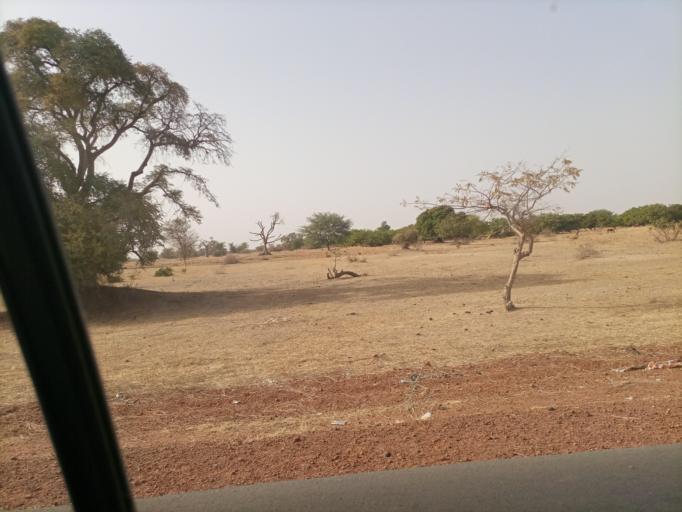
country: SN
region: Fatick
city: Foundiougne
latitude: 14.1295
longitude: -16.4064
